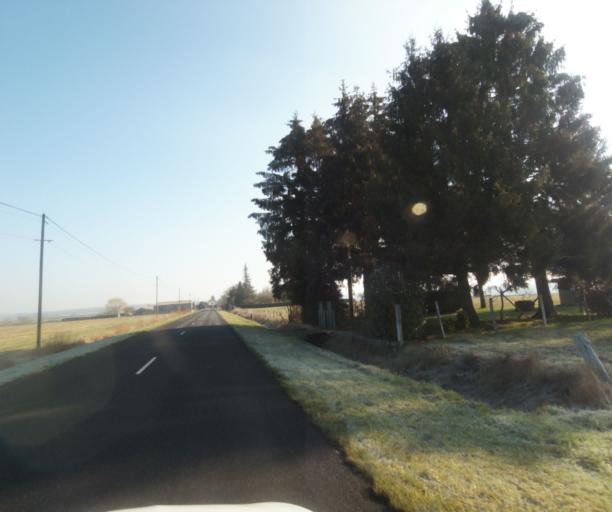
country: FR
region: Champagne-Ardenne
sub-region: Departement de la Haute-Marne
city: Laneuville-a-Remy
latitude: 48.4932
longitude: 4.8575
